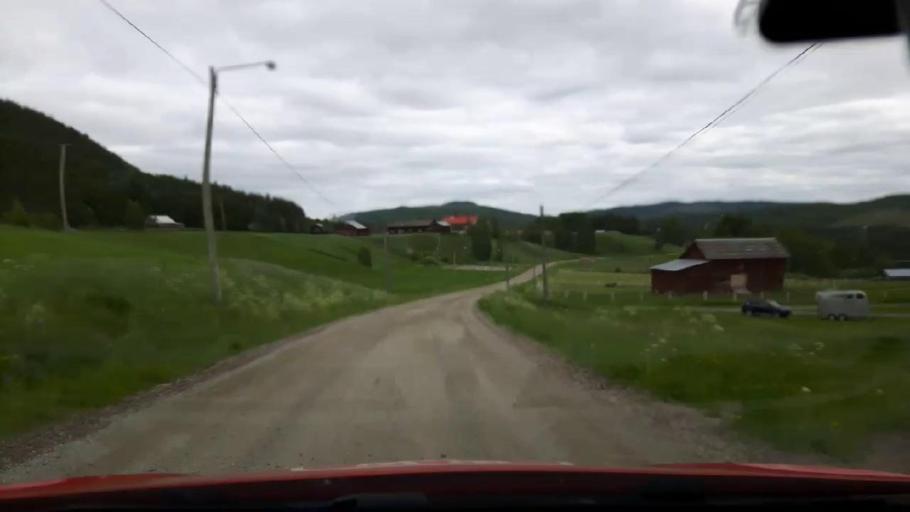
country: SE
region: Jaemtland
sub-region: Ragunda Kommun
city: Hammarstrand
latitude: 63.1662
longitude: 16.2139
